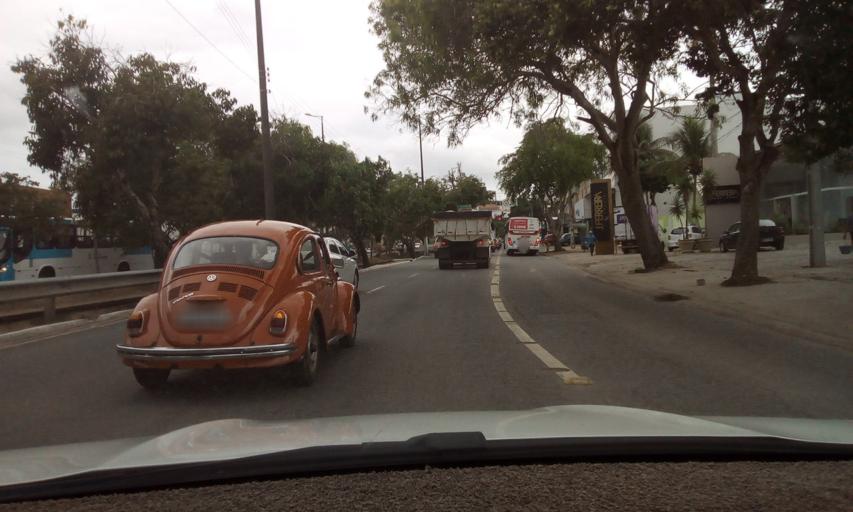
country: BR
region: Paraiba
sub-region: Campina Grande
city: Campina Grande
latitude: -7.2192
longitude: -35.8754
